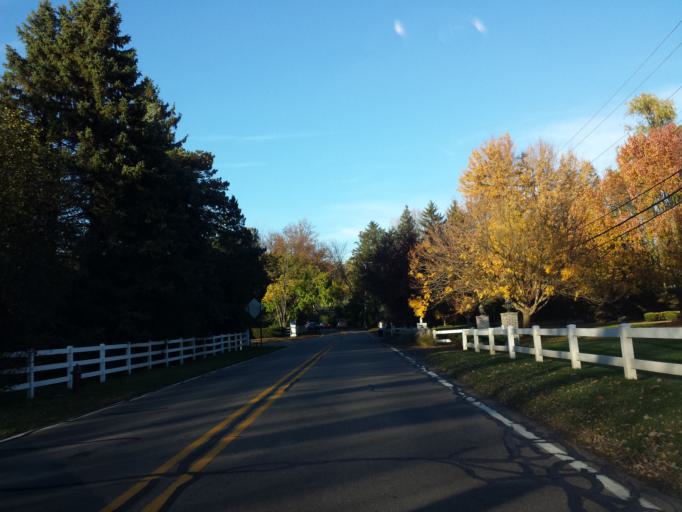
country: US
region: Michigan
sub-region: Oakland County
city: Beverly Hills
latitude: 42.5267
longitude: -83.2451
